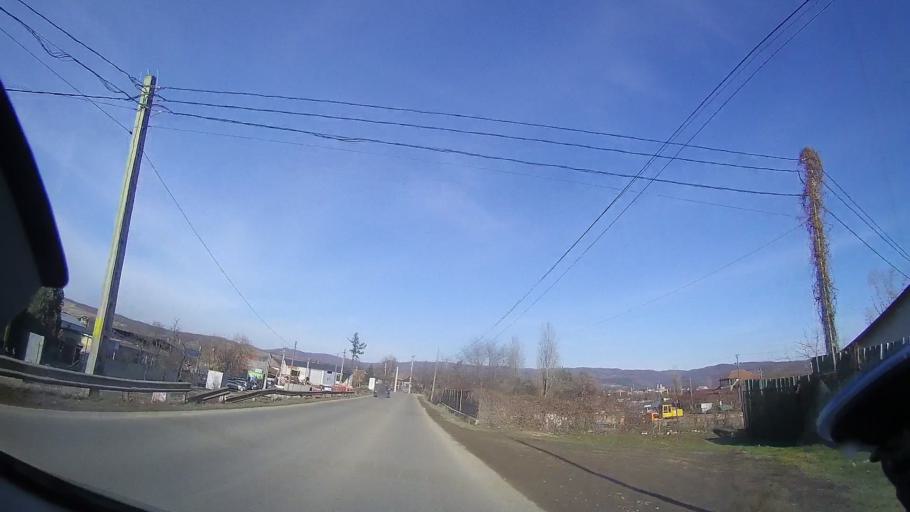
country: RO
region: Bihor
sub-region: Comuna Astileu
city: Astileu
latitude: 47.0491
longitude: 22.3920
